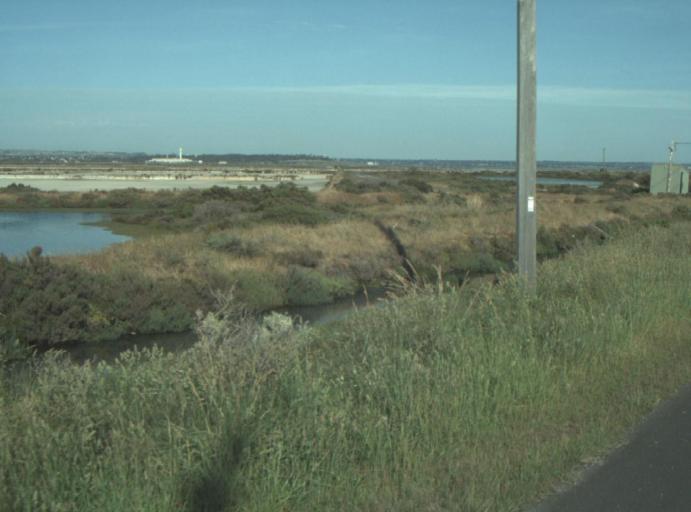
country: AU
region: Victoria
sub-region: Greater Geelong
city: Leopold
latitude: -38.1508
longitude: 144.4326
